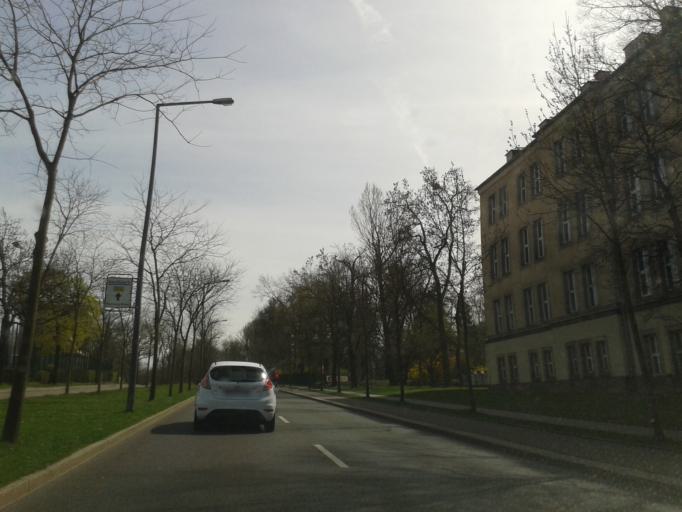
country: DE
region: Saxony
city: Dresden
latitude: 51.0307
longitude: 13.7512
